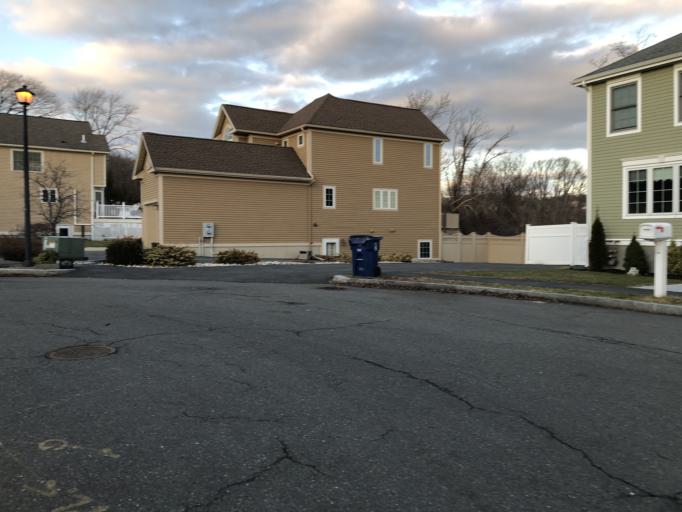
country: US
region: Massachusetts
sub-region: Essex County
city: Saugus
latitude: 42.4395
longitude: -71.0133
